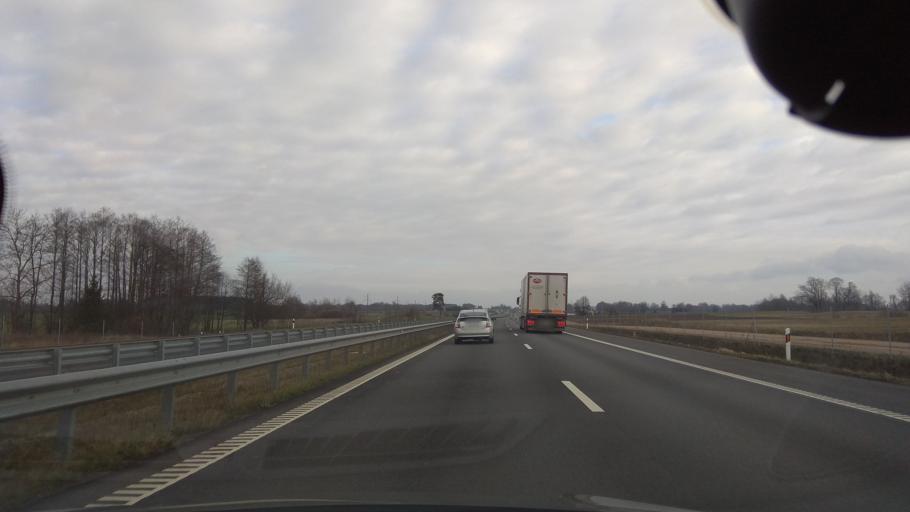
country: LT
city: Kazlu Ruda
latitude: 54.7120
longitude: 23.6415
